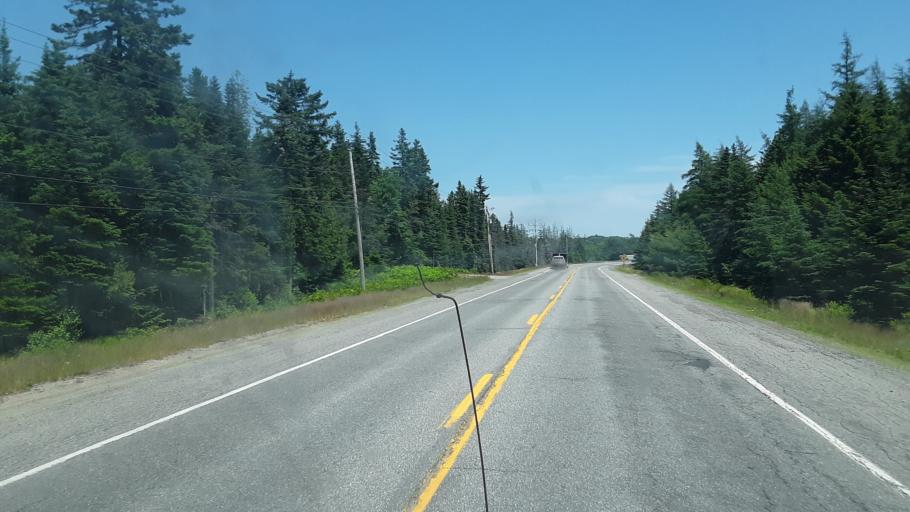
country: US
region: Maine
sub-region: Washington County
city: Steuben
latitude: 44.5123
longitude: -67.9717
